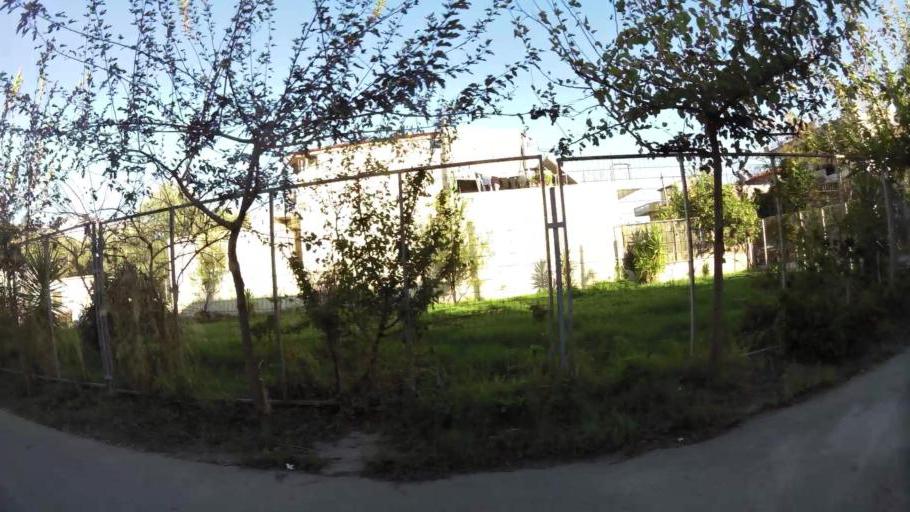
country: GR
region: Attica
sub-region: Nomarchia Anatolikis Attikis
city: Acharnes
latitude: 38.0818
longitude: 23.7294
